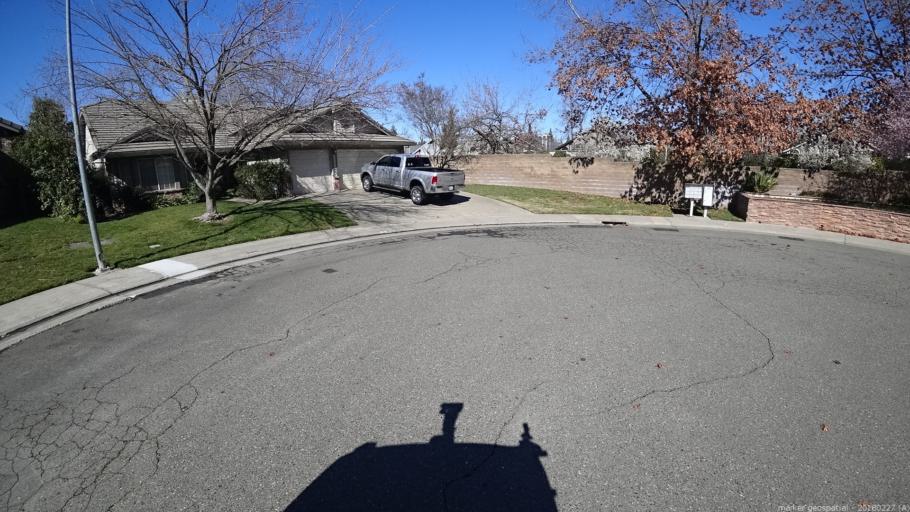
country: US
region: California
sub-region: Sacramento County
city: Antelope
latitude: 38.7181
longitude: -121.3500
